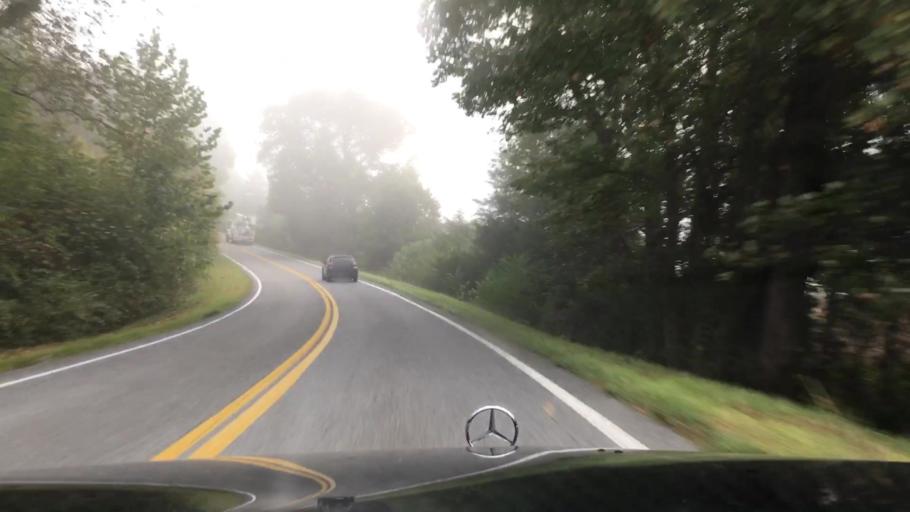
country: US
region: Virginia
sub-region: Campbell County
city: Timberlake
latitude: 37.2213
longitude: -79.2883
